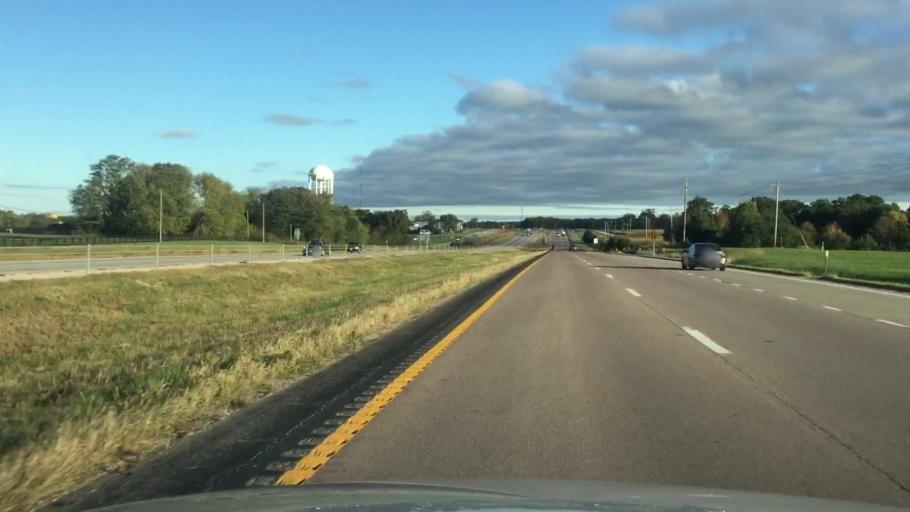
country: US
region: Missouri
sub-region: Boone County
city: Ashland
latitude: 38.8632
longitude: -92.2500
